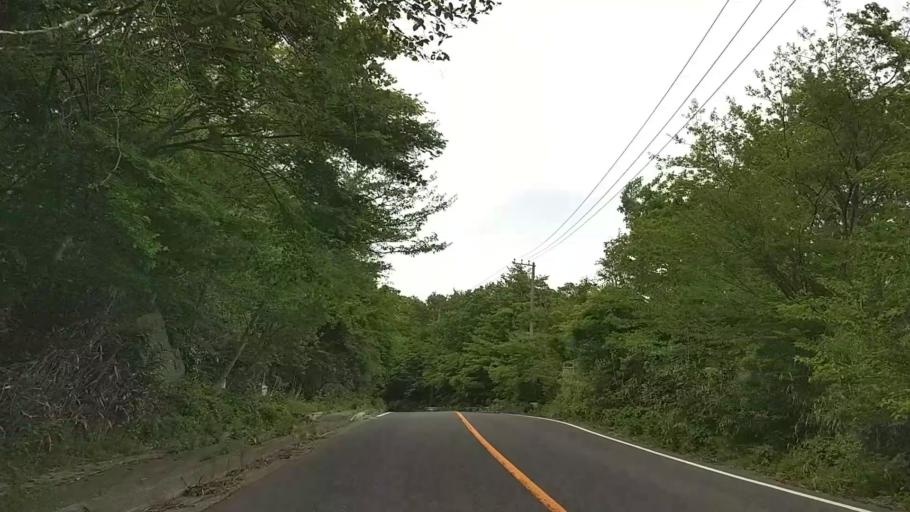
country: JP
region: Kanagawa
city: Hakone
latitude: 35.2440
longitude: 139.0394
